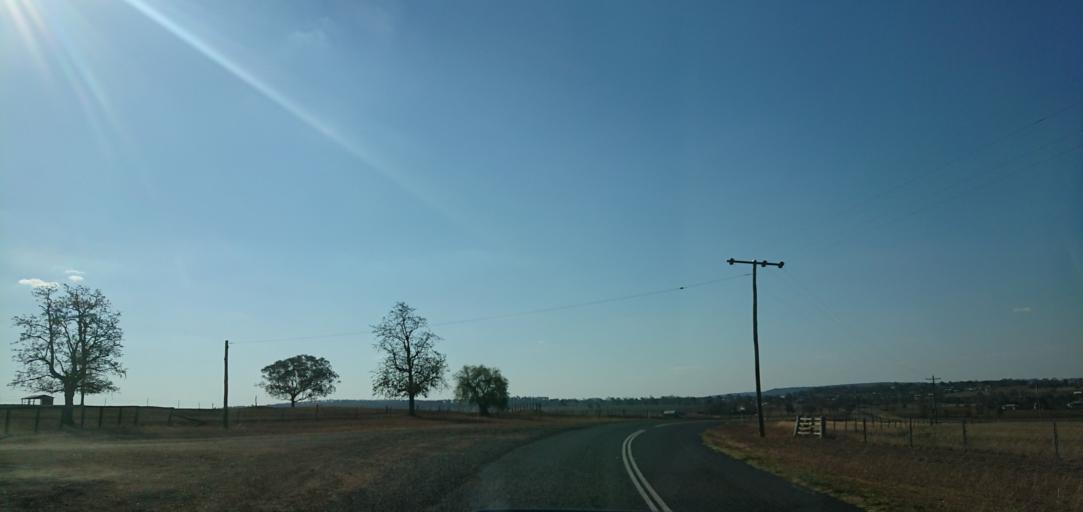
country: AU
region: Queensland
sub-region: Toowoomba
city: Westbrook
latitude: -27.6990
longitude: 151.7154
